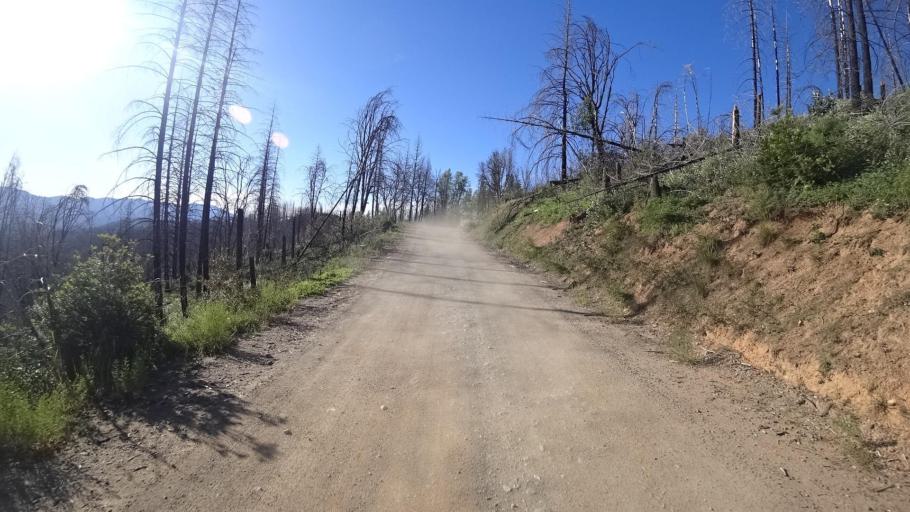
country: US
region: California
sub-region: Lake County
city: Upper Lake
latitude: 39.3393
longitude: -122.9583
